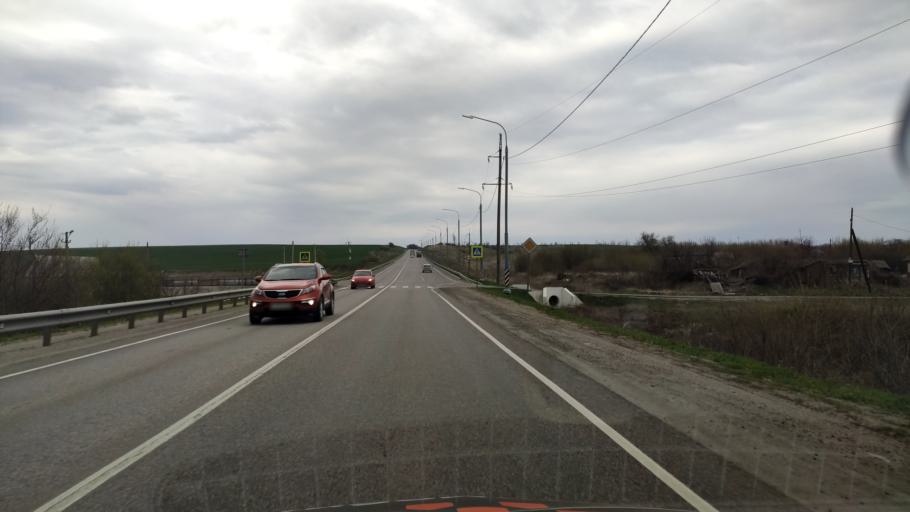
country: RU
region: Voronezj
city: Nizhnedevitsk
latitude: 51.5702
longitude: 38.4742
